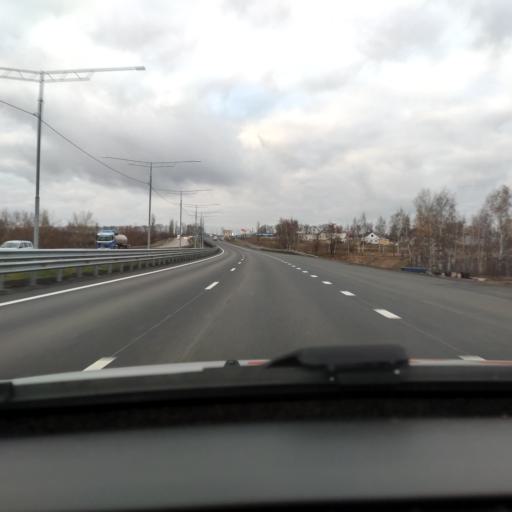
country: RU
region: Voronezj
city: Ramon'
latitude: 51.9758
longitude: 39.2205
